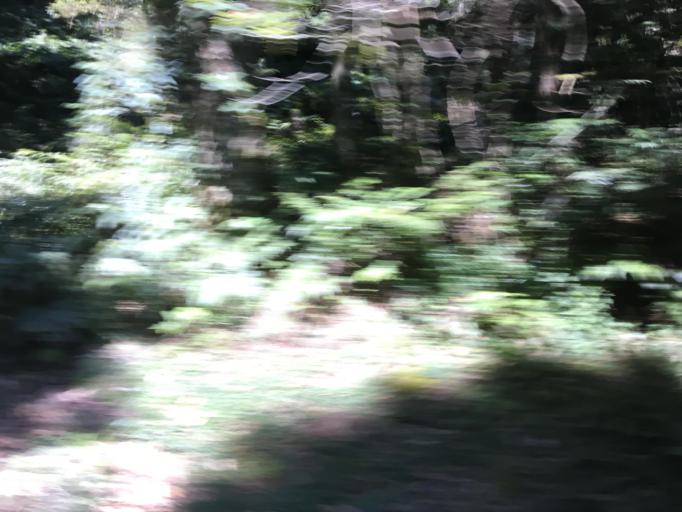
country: TW
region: Taiwan
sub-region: Yilan
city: Yilan
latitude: 24.5340
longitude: 121.5203
